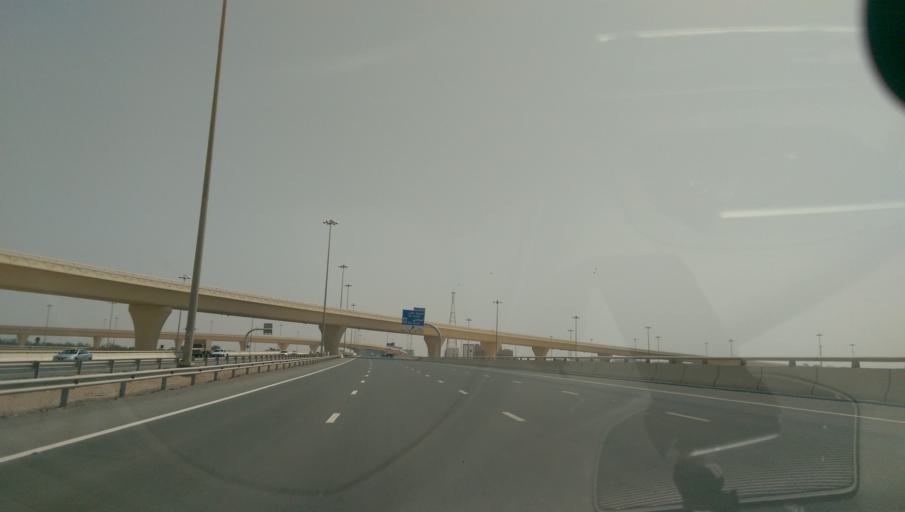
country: AE
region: Abu Dhabi
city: Abu Dhabi
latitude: 24.3063
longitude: 54.5994
